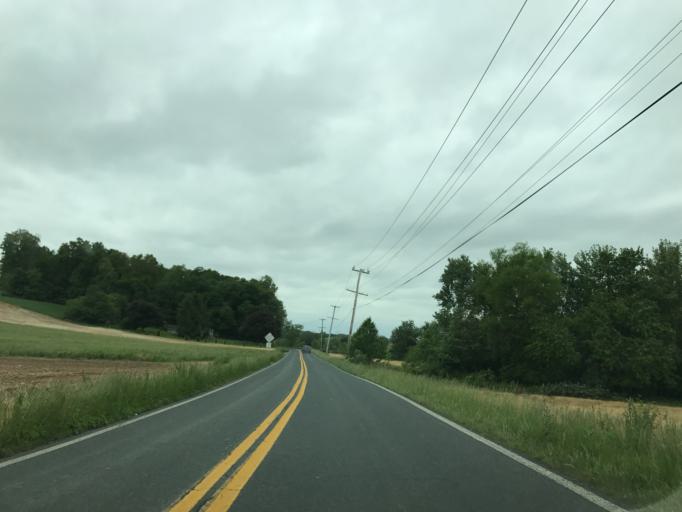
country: US
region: Maryland
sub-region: Carroll County
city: Manchester
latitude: 39.6343
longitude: -76.8697
